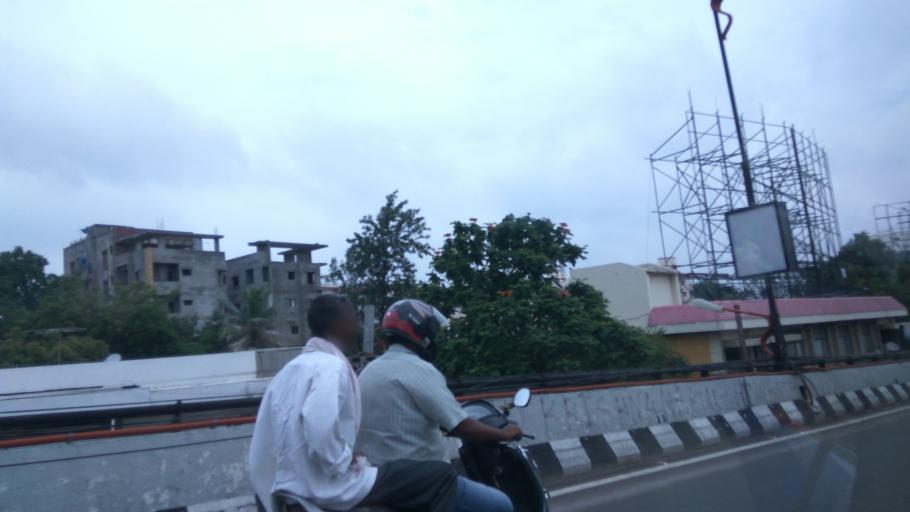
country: IN
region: Telangana
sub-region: Hyderabad
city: Hyderabad
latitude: 17.4363
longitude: 78.4560
